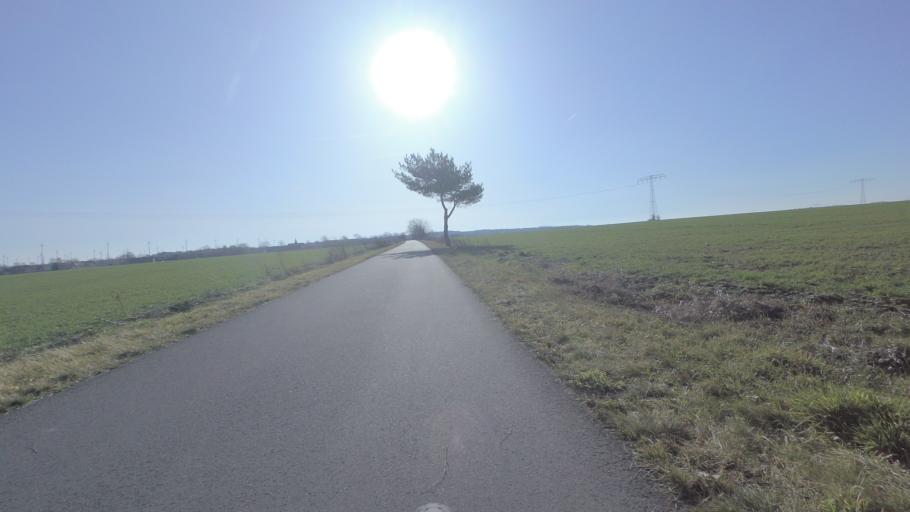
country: DE
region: Brandenburg
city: Luckenwalde
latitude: 52.0450
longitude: 13.1348
